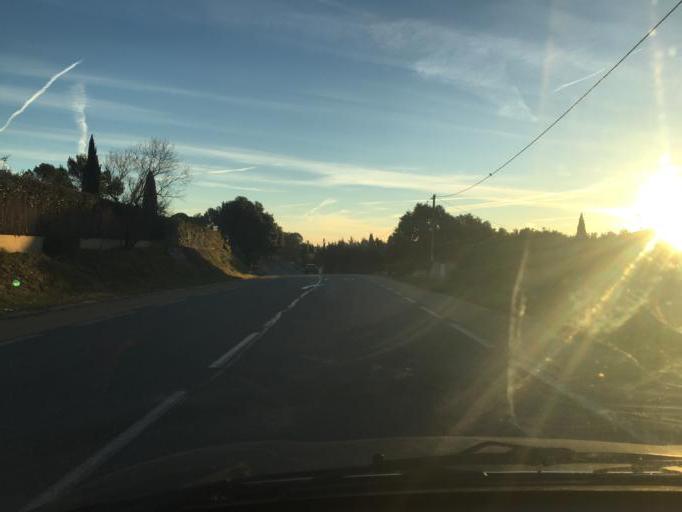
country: FR
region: Provence-Alpes-Cote d'Azur
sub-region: Departement du Var
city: Taradeau
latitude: 43.4489
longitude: 6.4380
